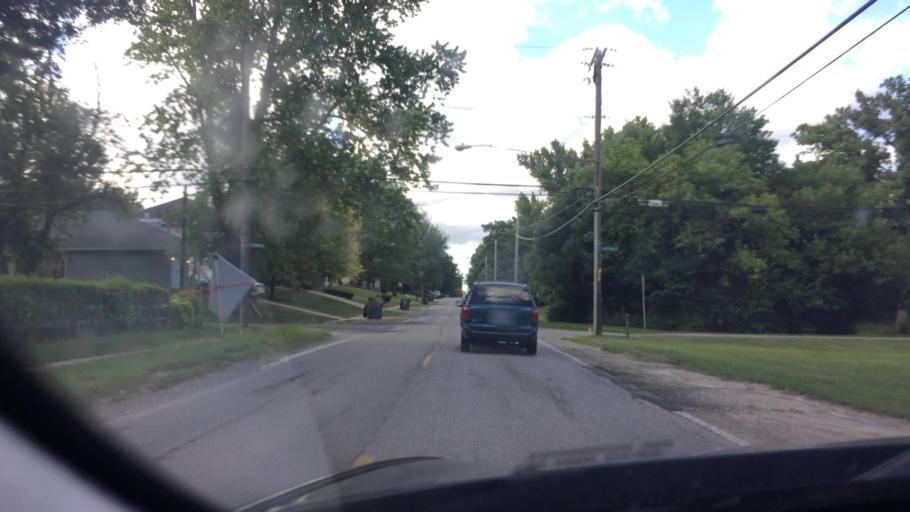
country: US
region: Ohio
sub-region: Lucas County
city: Ottawa Hills
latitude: 41.6493
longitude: -83.6407
